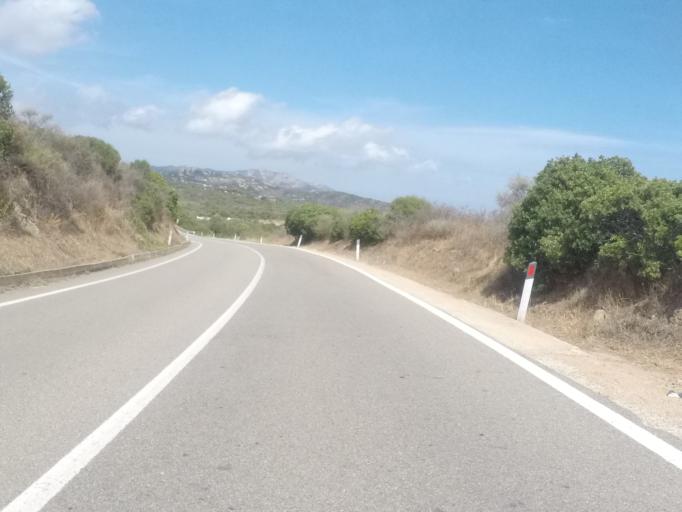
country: IT
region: Sardinia
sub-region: Provincia di Olbia-Tempio
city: Porto Cervo
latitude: 41.0449
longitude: 9.5187
